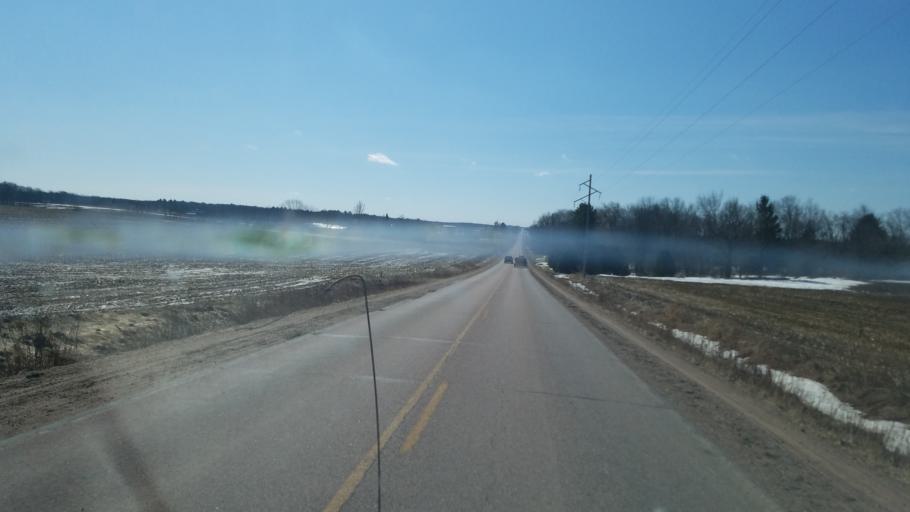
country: US
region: Wisconsin
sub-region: Clark County
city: Loyal
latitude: 44.5789
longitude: -90.3959
